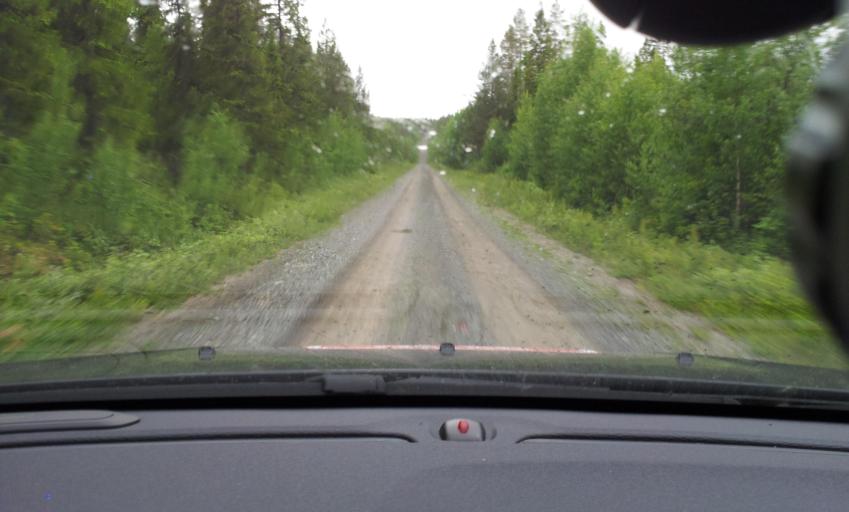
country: SE
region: Jaemtland
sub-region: Are Kommun
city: Jarpen
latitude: 63.1707
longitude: 13.5154
